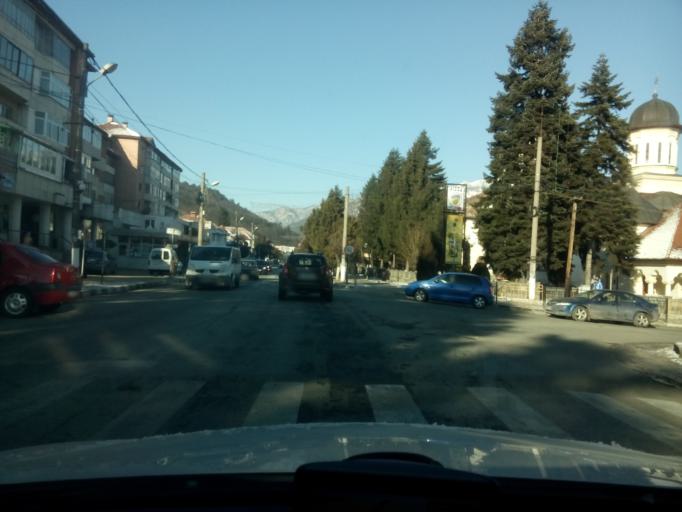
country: RO
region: Valcea
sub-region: Oras Calimanesti
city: Calimanesti
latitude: 45.2400
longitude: 24.3415
